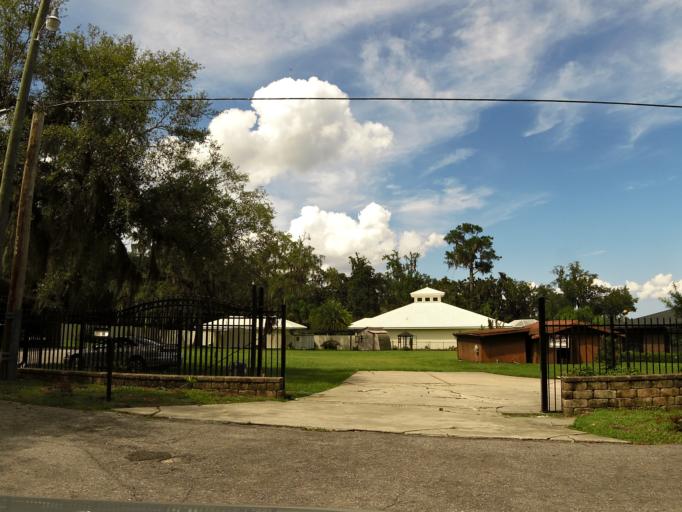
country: US
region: Florida
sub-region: Clay County
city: Lakeside
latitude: 30.1231
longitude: -81.7609
